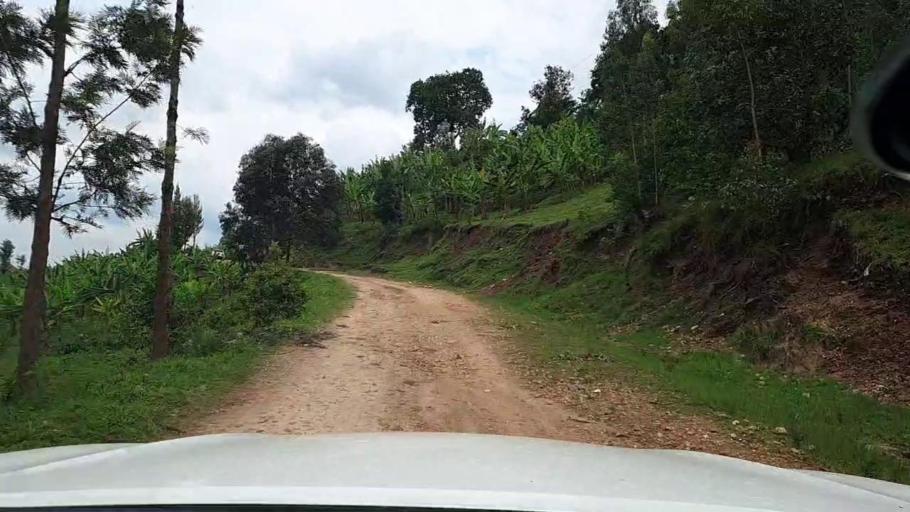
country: RW
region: Western Province
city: Kibuye
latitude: -2.0798
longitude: 29.4221
